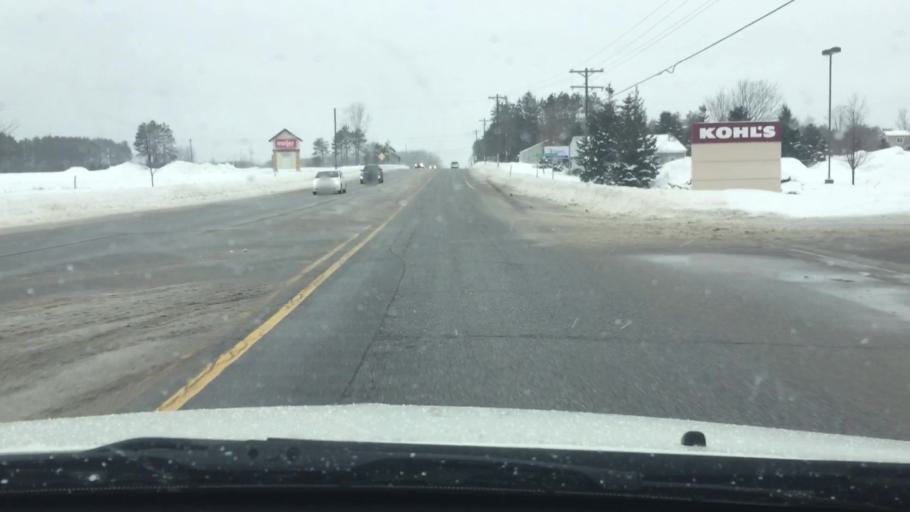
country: US
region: Michigan
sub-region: Otsego County
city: Gaylord
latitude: 45.0277
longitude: -84.7234
